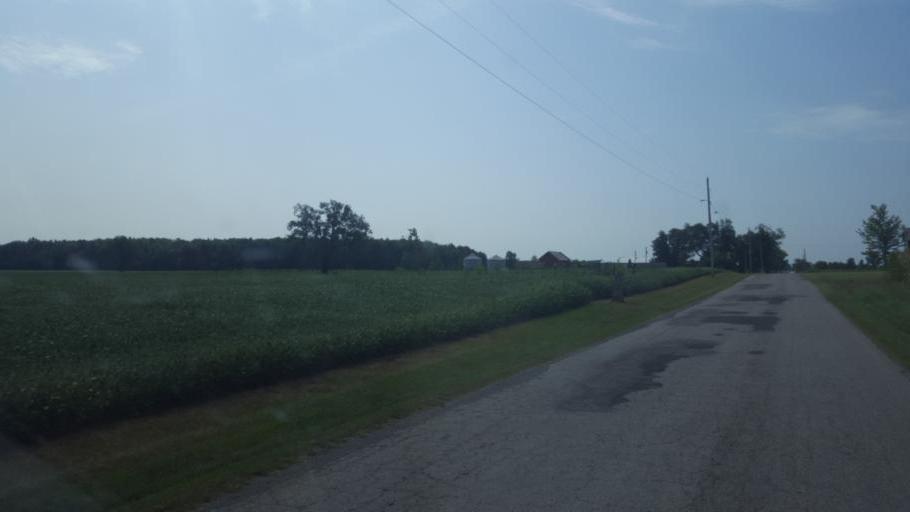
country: US
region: Ohio
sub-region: Delaware County
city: Ashley
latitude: 40.4673
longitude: -83.0080
